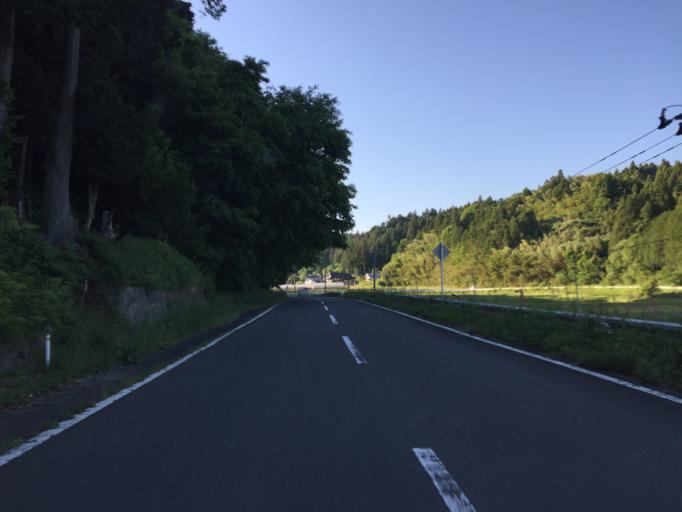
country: JP
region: Fukushima
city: Ishikawa
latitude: 36.9939
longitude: 140.4380
